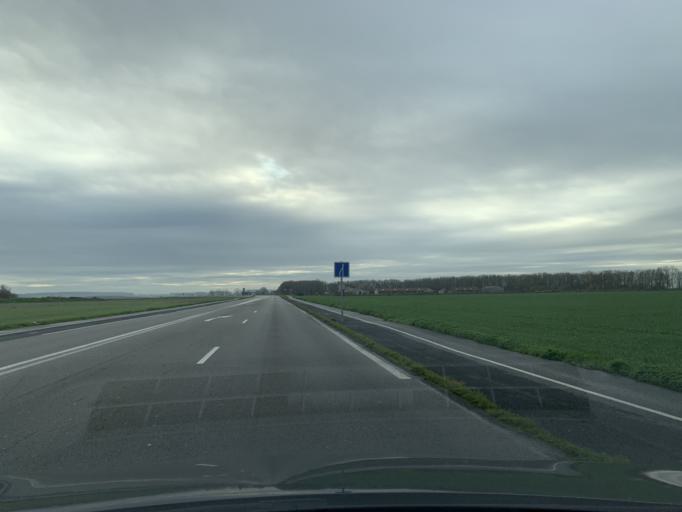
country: FR
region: Nord-Pas-de-Calais
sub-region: Departement du Nord
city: Goeulzin
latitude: 50.3330
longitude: 3.1036
